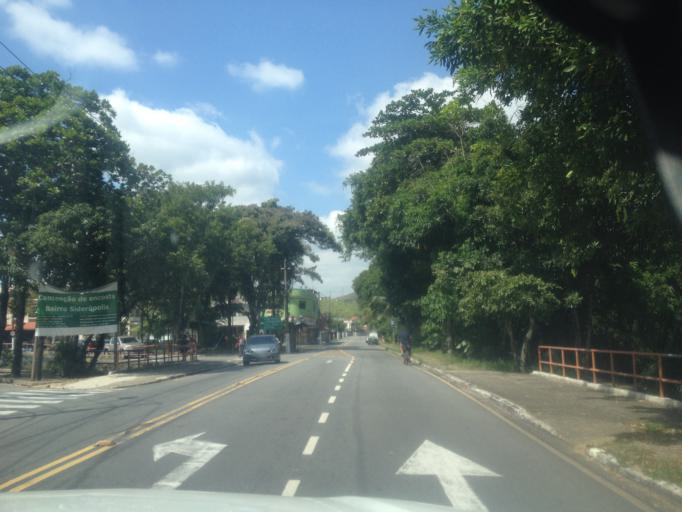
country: BR
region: Rio de Janeiro
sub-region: Volta Redonda
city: Volta Redonda
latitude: -22.5365
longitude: -44.0887
